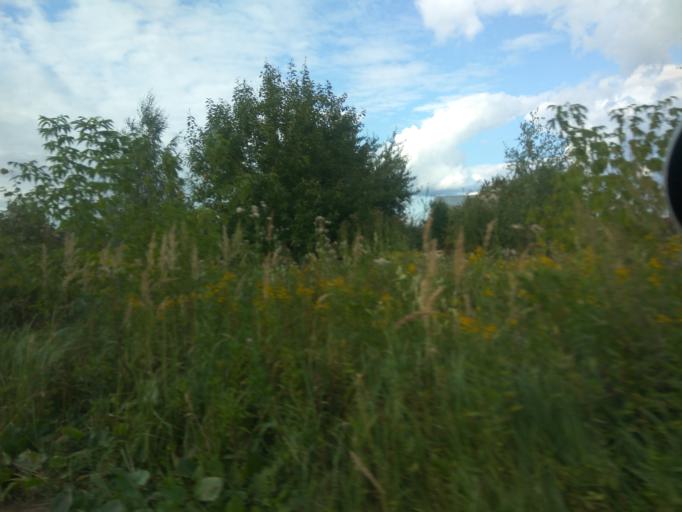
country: RU
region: Moskovskaya
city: Bronnitsy
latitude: 55.4720
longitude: 38.2624
